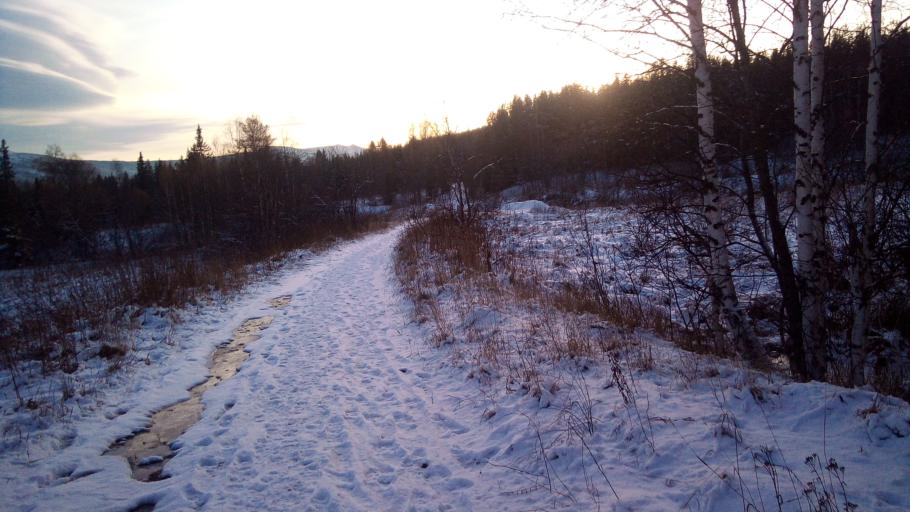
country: RU
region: Chelyabinsk
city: Satka
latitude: 54.8153
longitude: 59.0014
